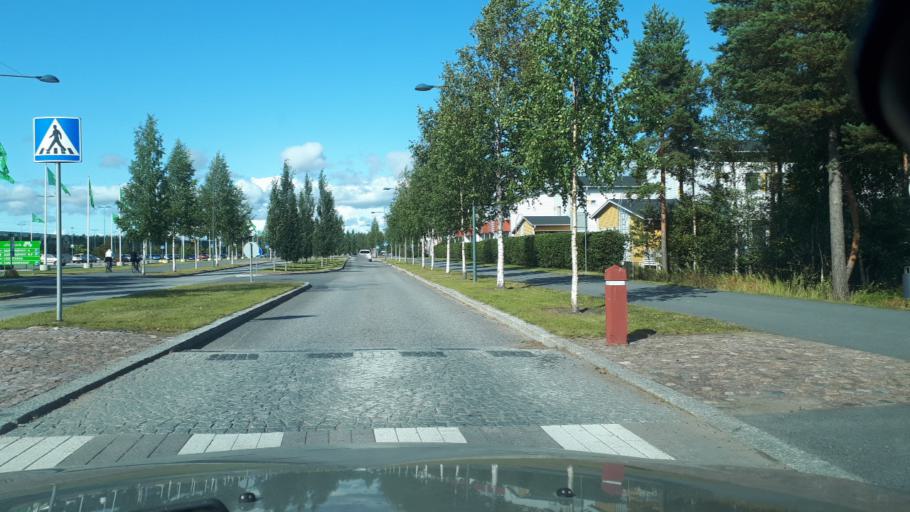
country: FI
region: Northern Ostrobothnia
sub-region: Oulu
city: Oulu
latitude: 65.0740
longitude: 25.4476
